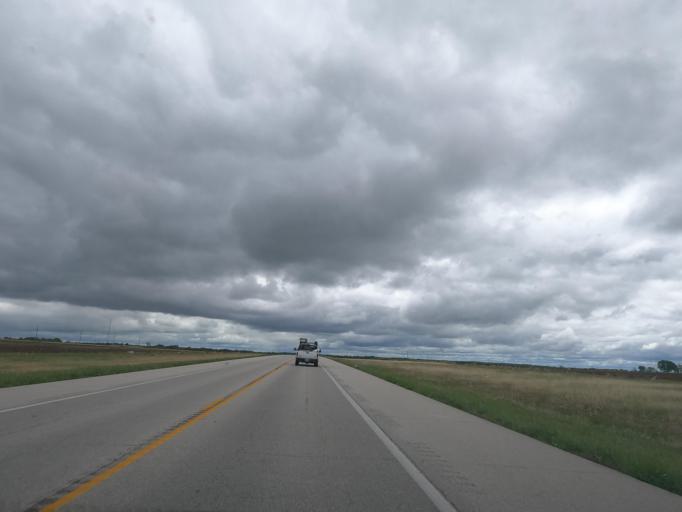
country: US
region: Kansas
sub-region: Wilson County
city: Fredonia
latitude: 37.4993
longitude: -95.7661
